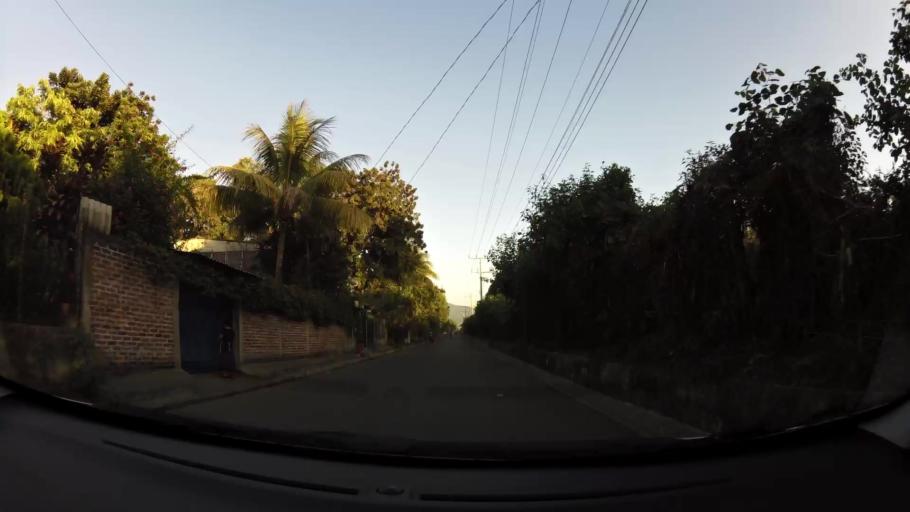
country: SV
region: Sonsonate
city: Armenia
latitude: 13.7412
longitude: -89.3968
